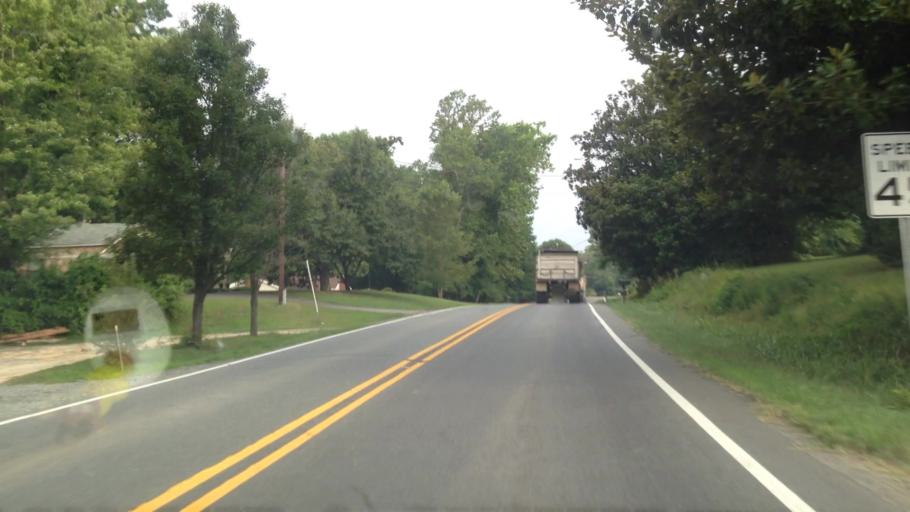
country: US
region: North Carolina
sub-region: Forsyth County
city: Walkertown
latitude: 36.1754
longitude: -80.1733
